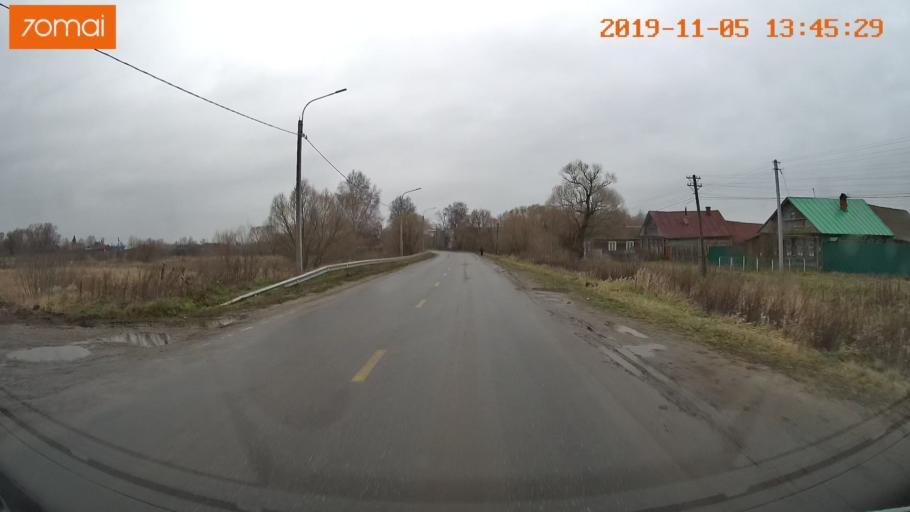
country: RU
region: Ivanovo
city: Shuya
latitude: 56.9890
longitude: 41.4124
